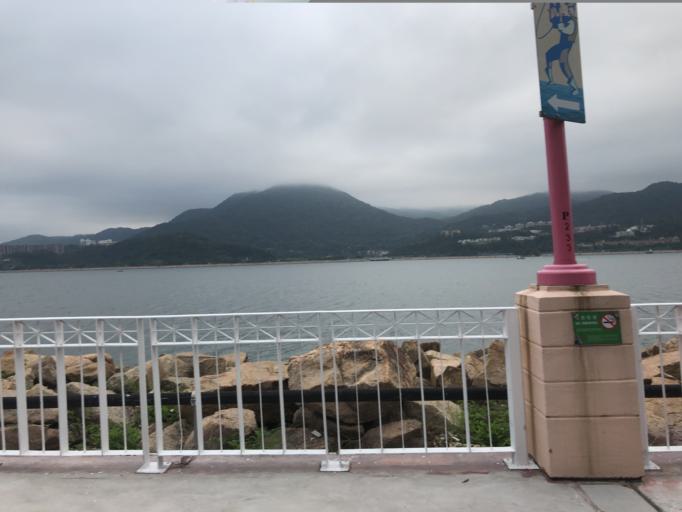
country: HK
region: Tai Po
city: Tai Po
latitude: 22.4513
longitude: 114.1919
